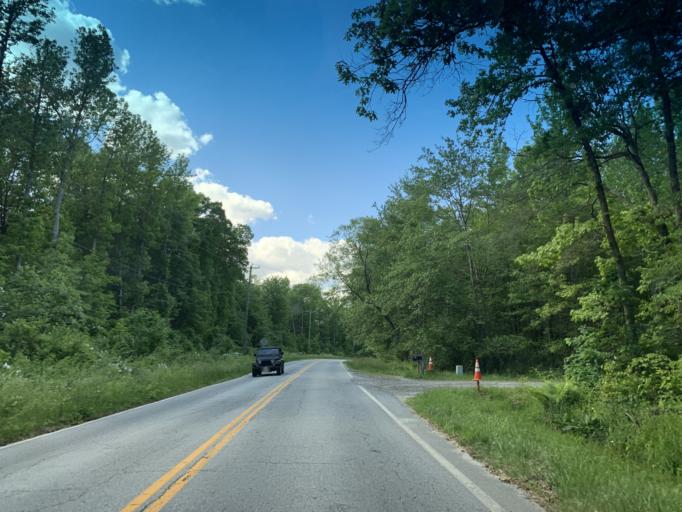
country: US
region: Maryland
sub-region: Cecil County
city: North East
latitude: 39.5761
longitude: -75.9424
